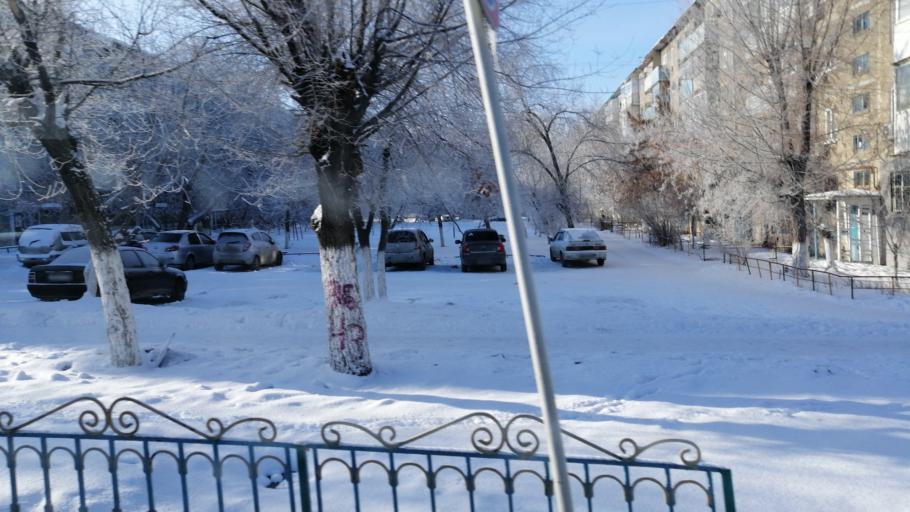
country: KZ
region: Aqtoebe
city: Aqtobe
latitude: 50.3054
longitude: 57.1508
